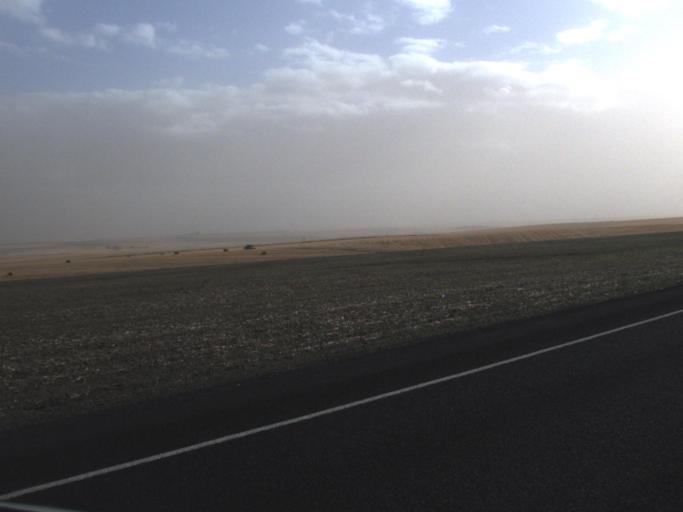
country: US
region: Washington
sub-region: Lincoln County
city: Davenport
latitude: 47.4529
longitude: -118.3130
